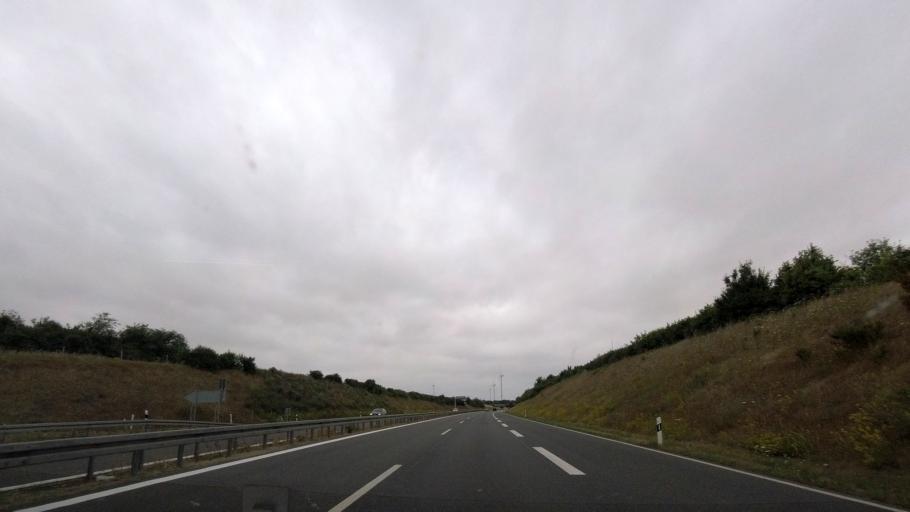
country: DE
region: Brandenburg
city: Schenkenberg
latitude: 53.3565
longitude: 13.9743
